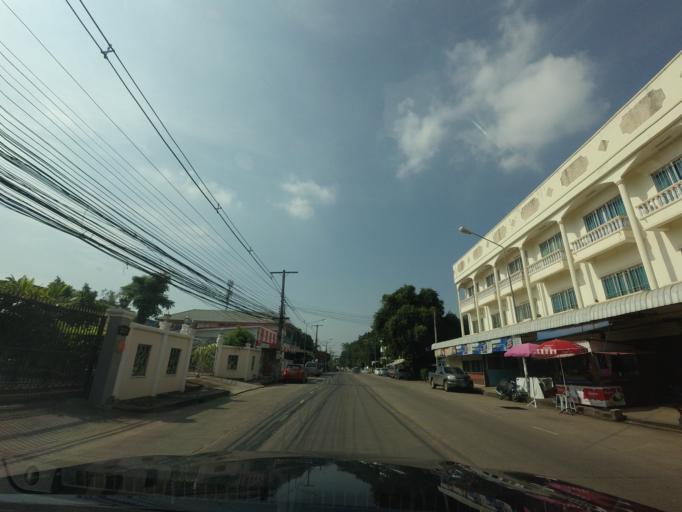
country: TH
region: Khon Kaen
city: Khon Kaen
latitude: 16.4228
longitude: 102.8500
